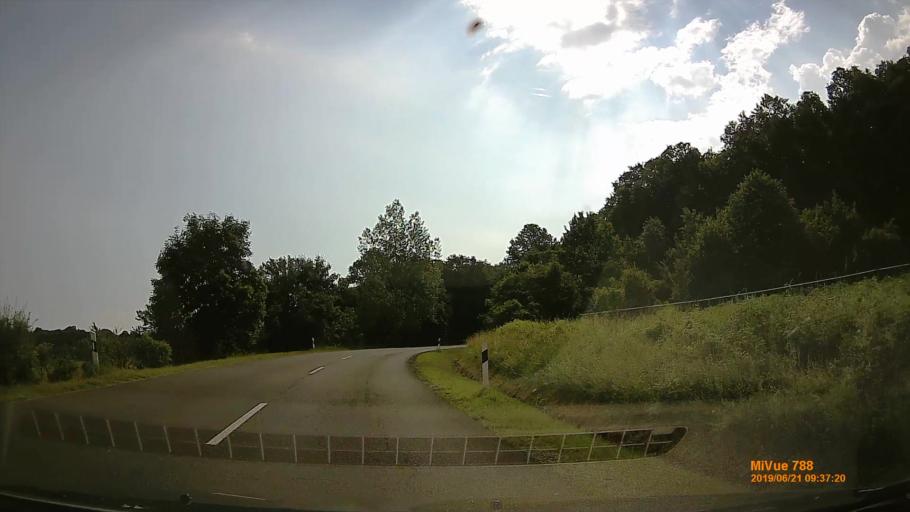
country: HU
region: Somogy
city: Taszar
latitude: 46.3150
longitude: 17.9151
